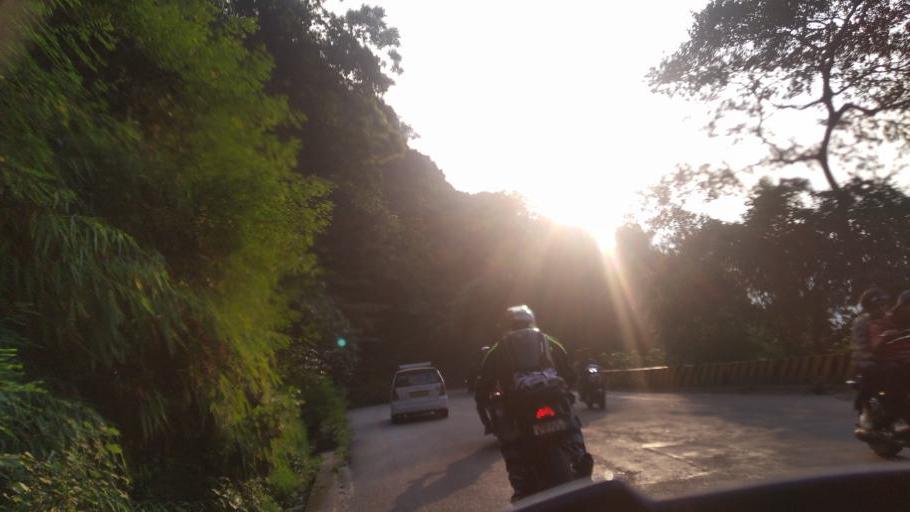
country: IN
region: Kerala
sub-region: Wayanad
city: Kalpetta
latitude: 11.5056
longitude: 76.0308
